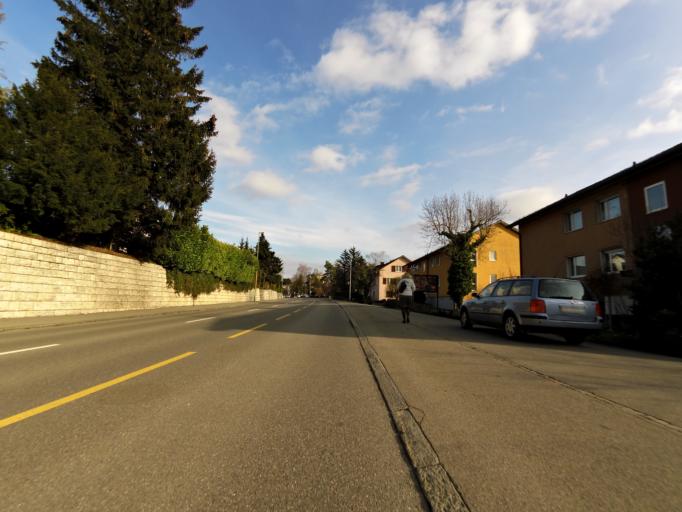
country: CH
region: Zurich
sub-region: Bezirk Dietikon
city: Oberengstringen
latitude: 47.4059
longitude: 8.4724
